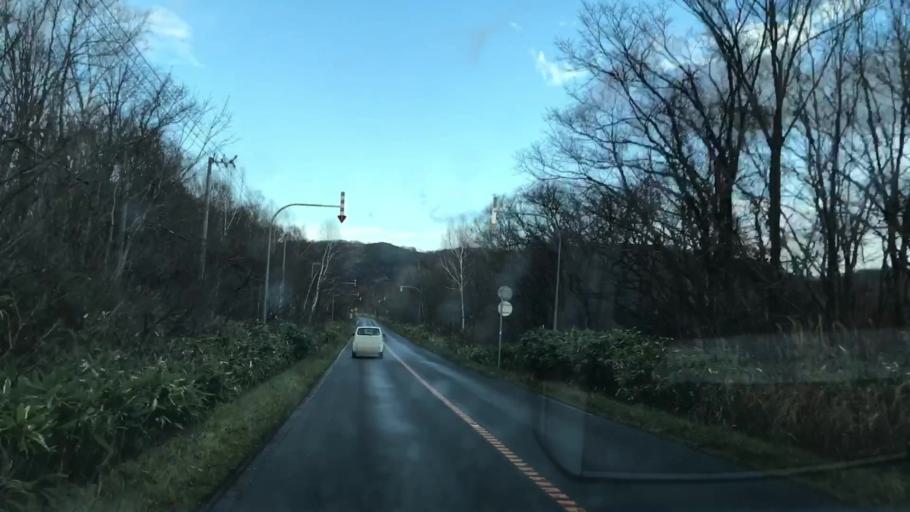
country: JP
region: Hokkaido
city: Yoichi
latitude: 43.3255
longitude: 140.5015
